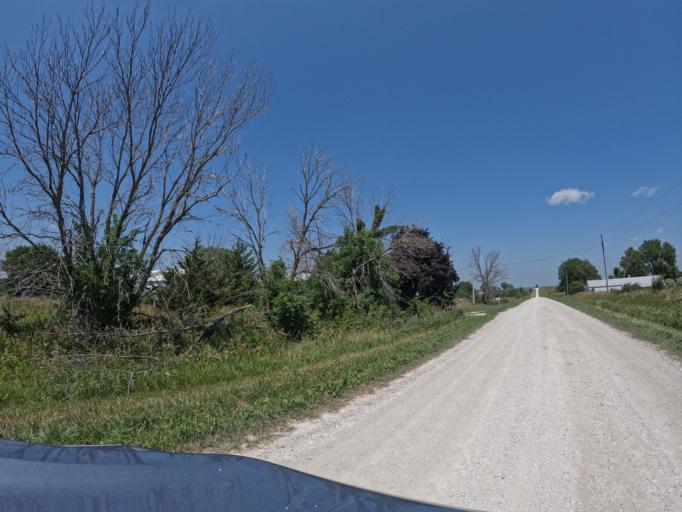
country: US
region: Iowa
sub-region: Keokuk County
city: Sigourney
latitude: 41.2688
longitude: -92.1701
